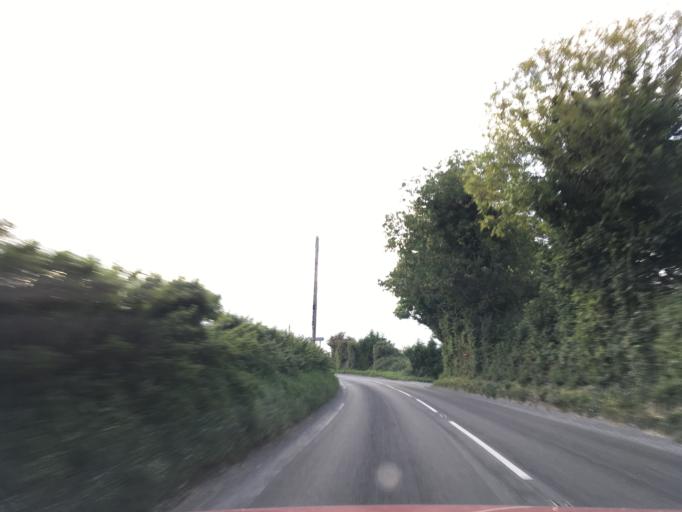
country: GB
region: England
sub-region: Wiltshire
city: Market Lavington
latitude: 51.3172
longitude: -1.9185
